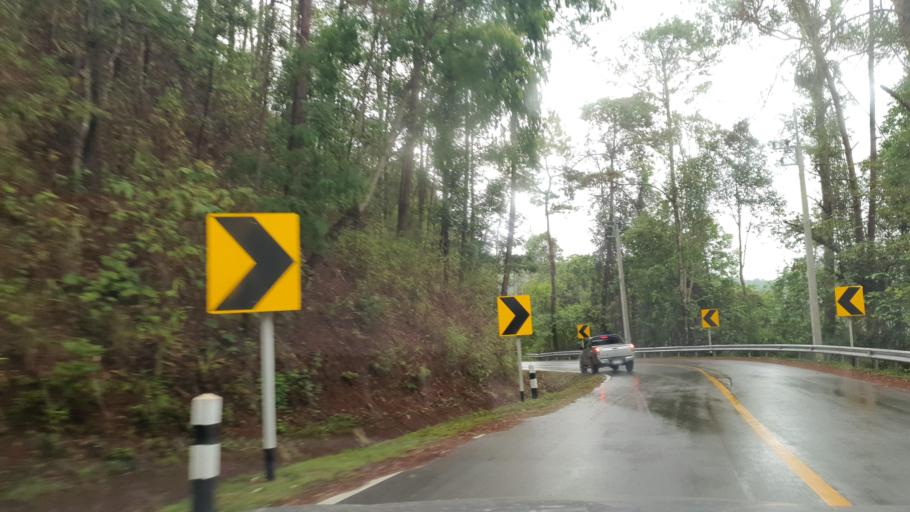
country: TH
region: Mae Hong Son
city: Mae Hi
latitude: 19.2519
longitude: 98.6420
